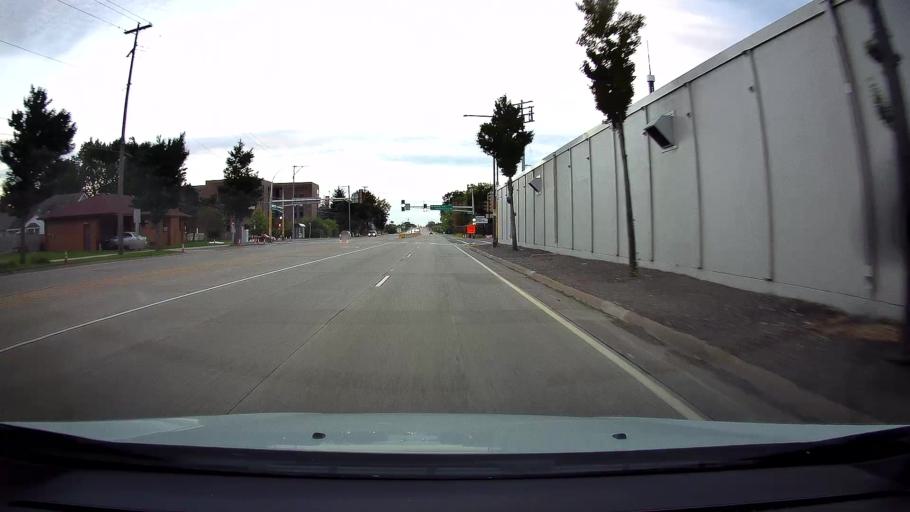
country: US
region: Minnesota
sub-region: Ramsey County
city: Falcon Heights
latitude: 44.9818
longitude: -93.1671
